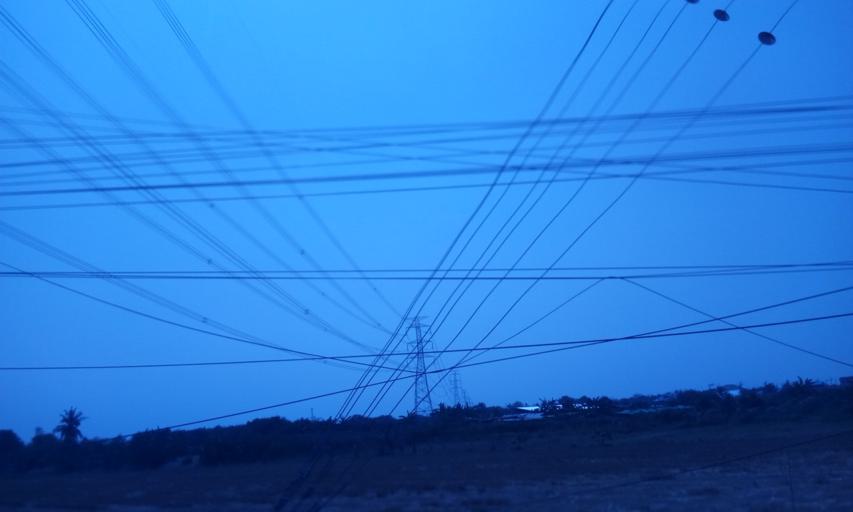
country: TH
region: Nonthaburi
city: Sai Noi
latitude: 13.9646
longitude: 100.3106
